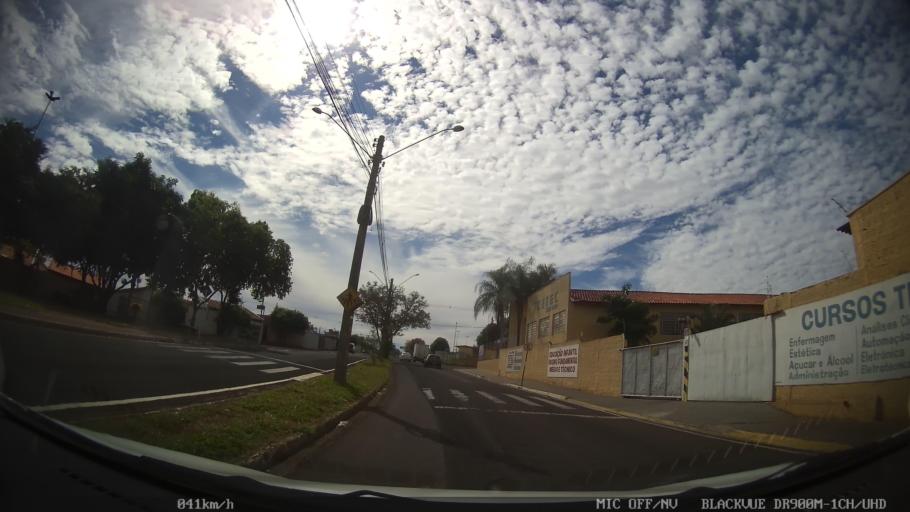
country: BR
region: Sao Paulo
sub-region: Catanduva
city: Catanduva
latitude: -21.1473
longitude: -48.9476
